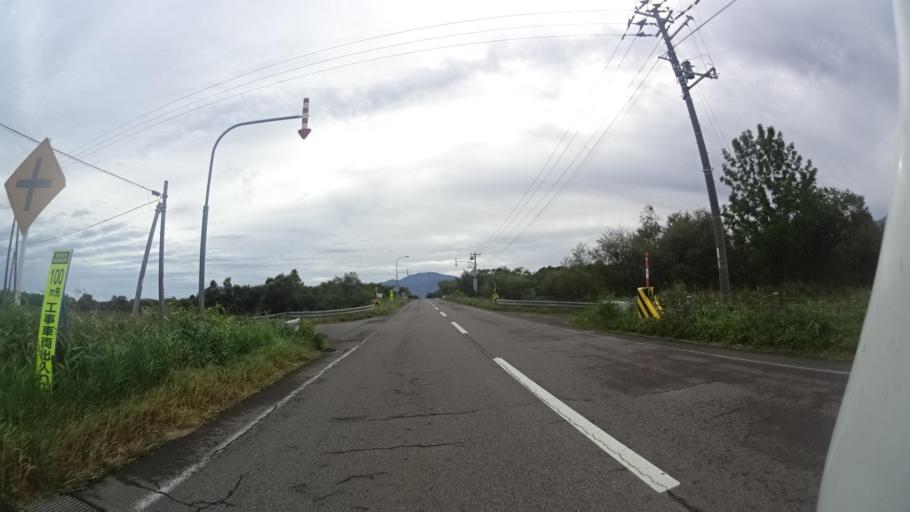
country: JP
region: Hokkaido
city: Abashiri
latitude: 43.8709
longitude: 144.6690
